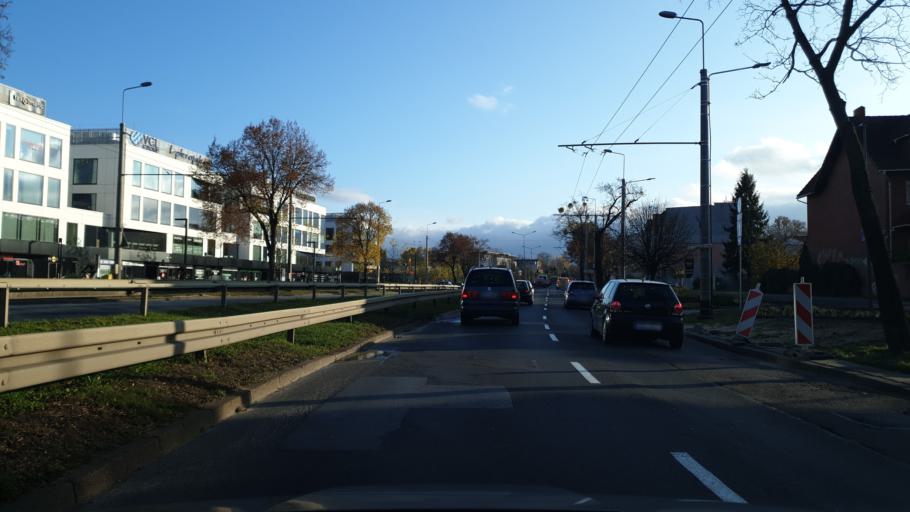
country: PL
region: Pomeranian Voivodeship
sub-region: Sopot
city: Sopot
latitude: 54.4815
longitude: 18.5511
